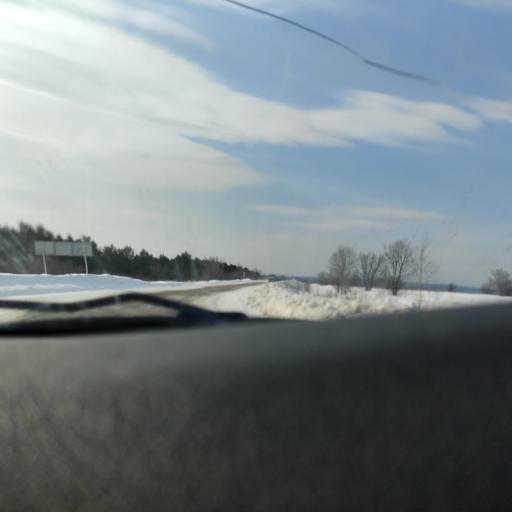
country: RU
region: Samara
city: Rozhdestveno
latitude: 53.2483
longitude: 49.9903
